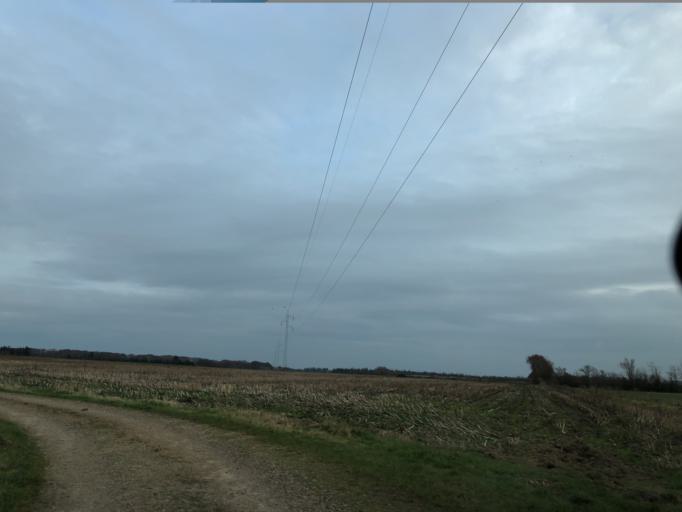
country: DK
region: Central Jutland
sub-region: Holstebro Kommune
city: Ulfborg
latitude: 56.2755
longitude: 8.2207
